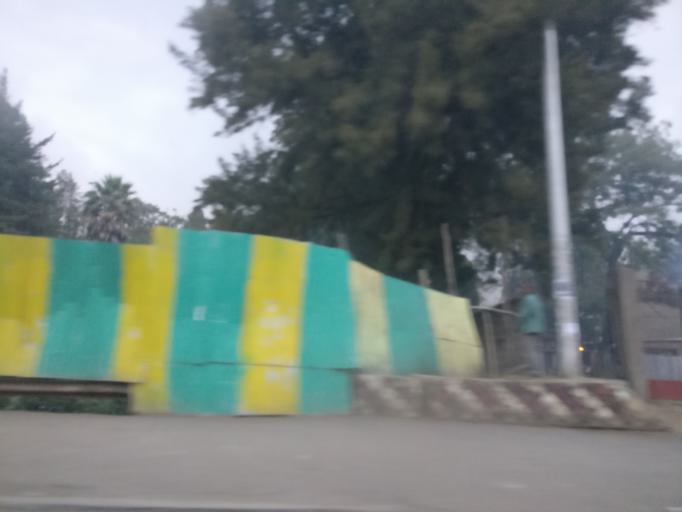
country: ET
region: Adis Abeba
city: Addis Ababa
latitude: 9.0175
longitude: 38.7554
